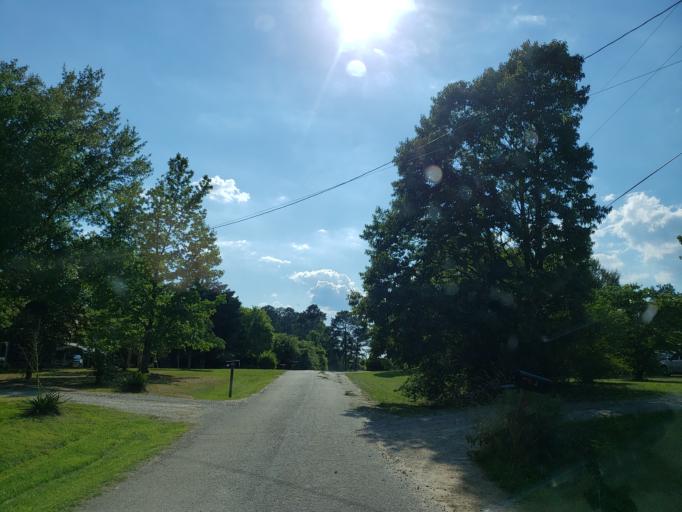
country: US
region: Georgia
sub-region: Haralson County
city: Buchanan
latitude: 33.8072
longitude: -85.1006
